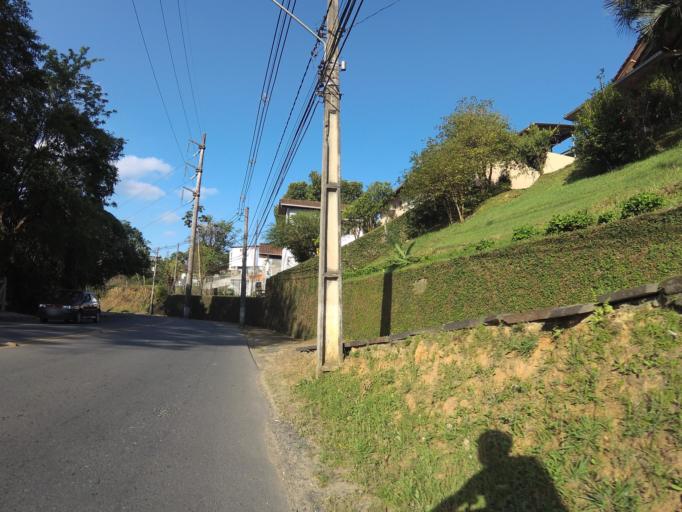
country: BR
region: Santa Catarina
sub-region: Blumenau
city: Blumenau
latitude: -26.9254
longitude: -49.1090
